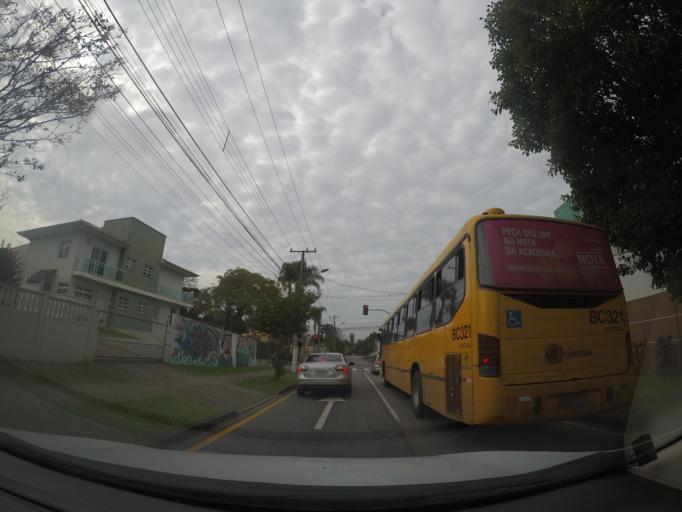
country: BR
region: Parana
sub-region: Curitiba
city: Curitiba
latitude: -25.4169
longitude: -49.2771
